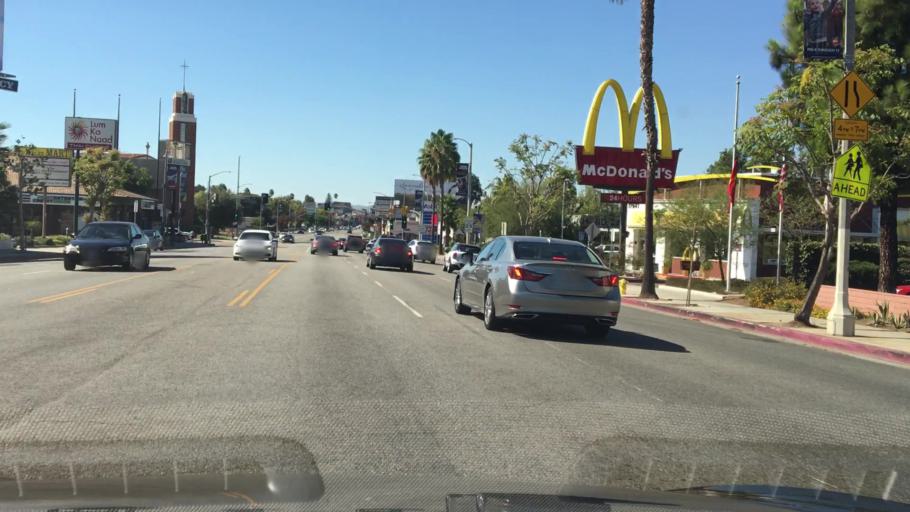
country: US
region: California
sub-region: Los Angeles County
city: Sherman Oaks
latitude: 34.1622
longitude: -118.5172
